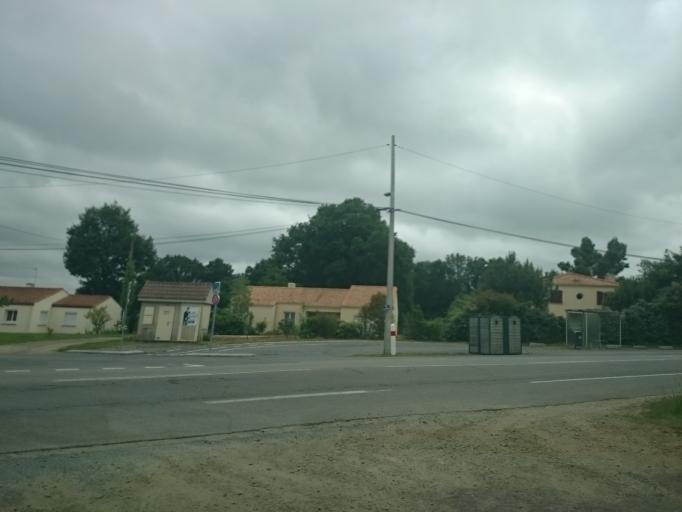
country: FR
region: Pays de la Loire
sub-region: Departement de la Loire-Atlantique
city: Bouaye
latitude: 47.1421
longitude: -1.7047
